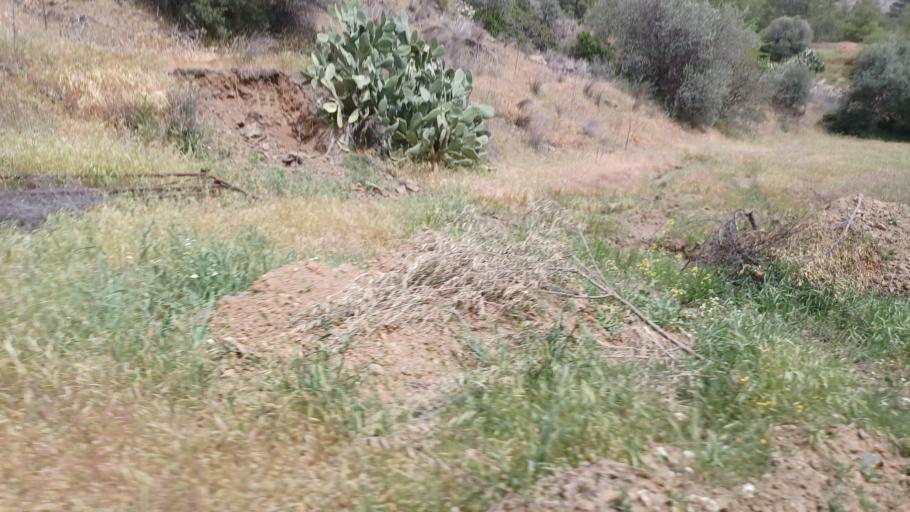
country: CY
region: Limassol
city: Parekklisha
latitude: 34.8475
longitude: 33.1025
